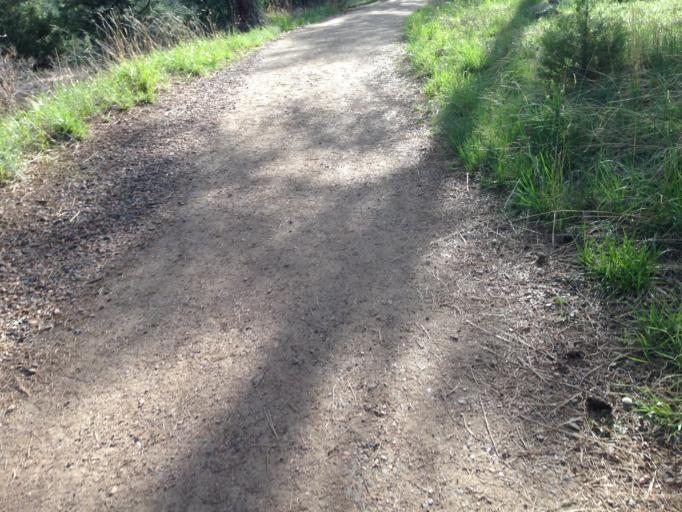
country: US
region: Colorado
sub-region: Boulder County
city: Boulder
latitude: 39.9445
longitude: -105.2768
